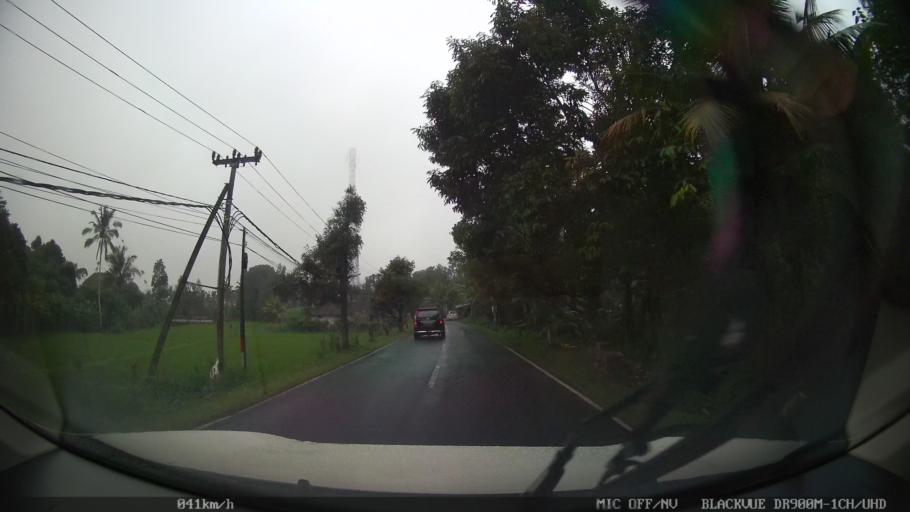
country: ID
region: Bali
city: Banjar Taro Kelod
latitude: -8.3599
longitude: 115.2729
